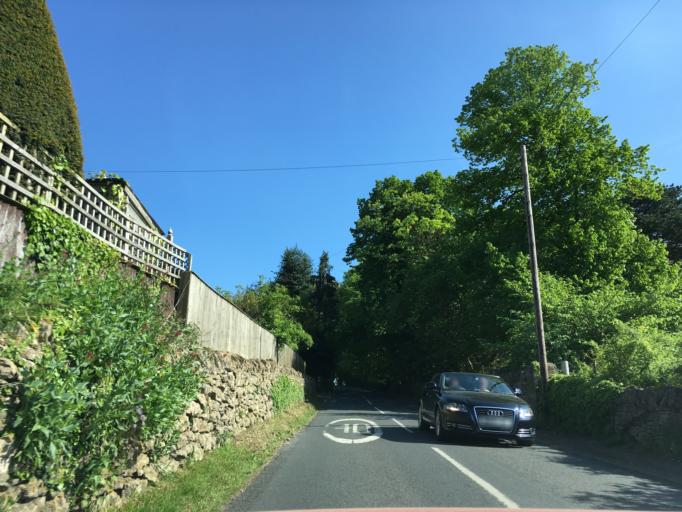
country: GB
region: England
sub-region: Gloucestershire
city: Nailsworth
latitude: 51.7144
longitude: -2.2283
